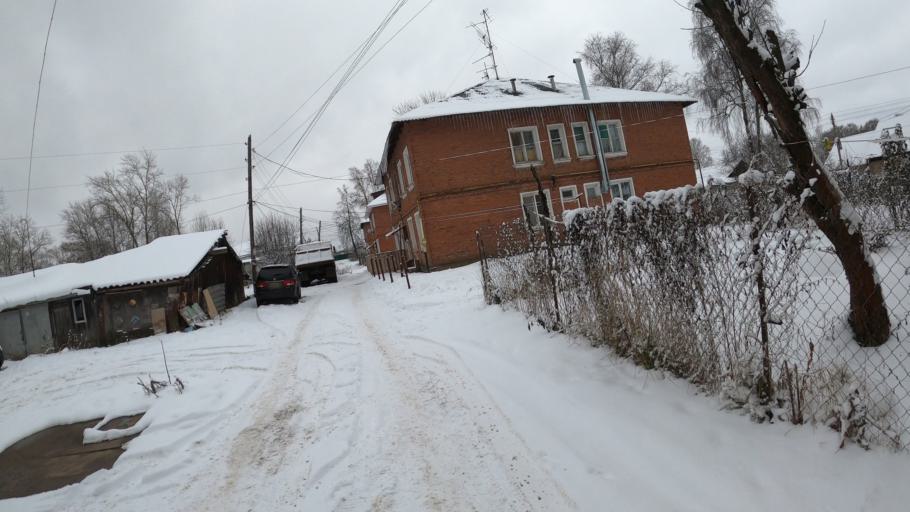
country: RU
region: Jaroslavl
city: Pereslavl'-Zalesskiy
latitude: 56.7504
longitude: 38.8638
